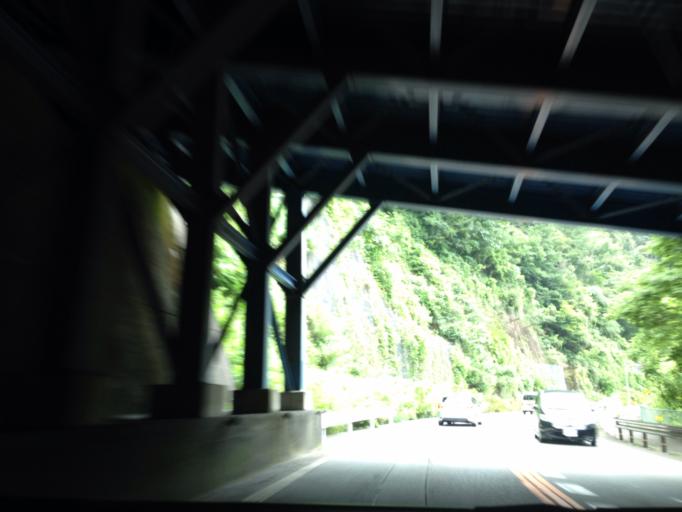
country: JP
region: Gifu
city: Gujo
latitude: 35.7512
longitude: 137.2103
